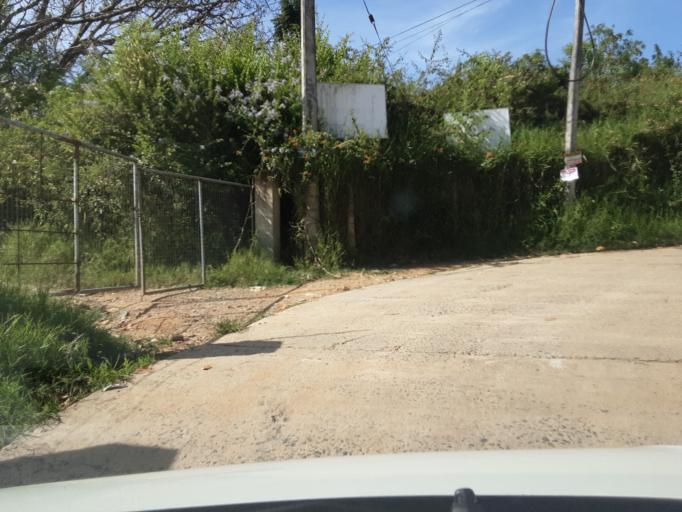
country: LK
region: Uva
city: Haputale
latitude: 6.8939
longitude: 80.9210
